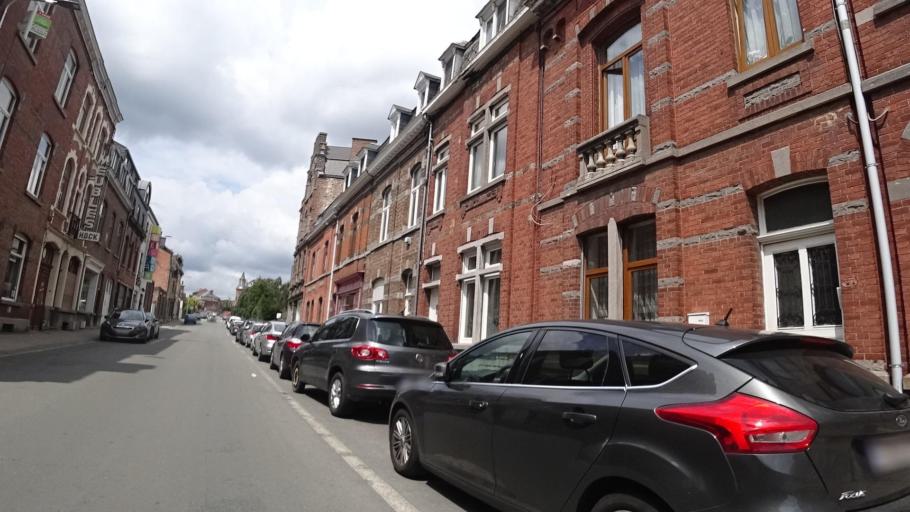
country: BE
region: Wallonia
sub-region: Province de Namur
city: Namur
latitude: 50.4707
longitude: 4.8584
